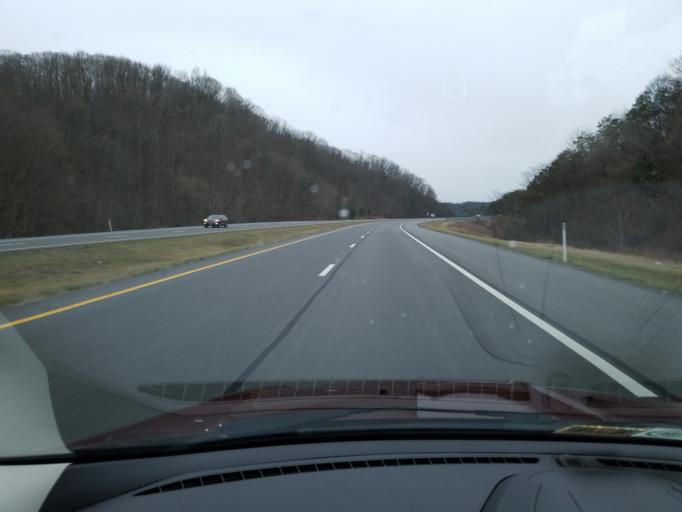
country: US
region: West Virginia
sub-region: Mercer County
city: Athens
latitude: 37.3402
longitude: -80.9667
